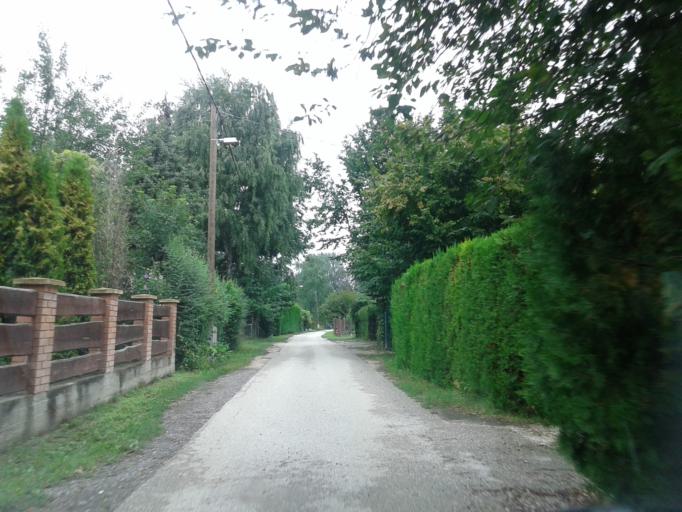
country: HU
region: Bacs-Kiskun
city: Harta
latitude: 46.6810
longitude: 18.9995
